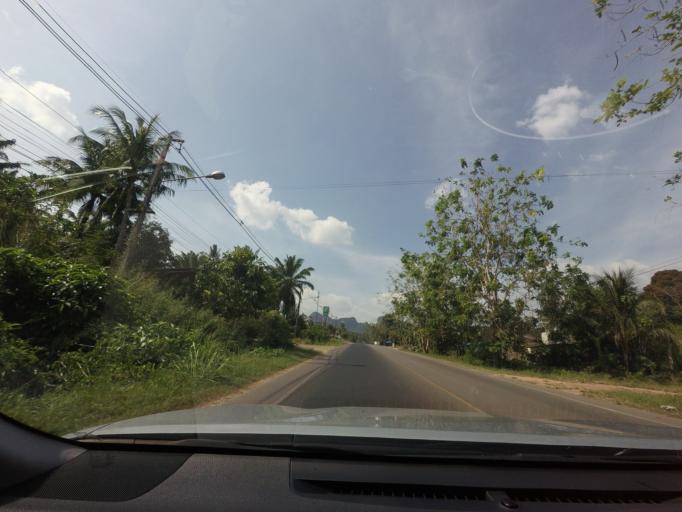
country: TH
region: Phangnga
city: Ban Ao Nang
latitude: 8.0979
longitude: 98.8030
